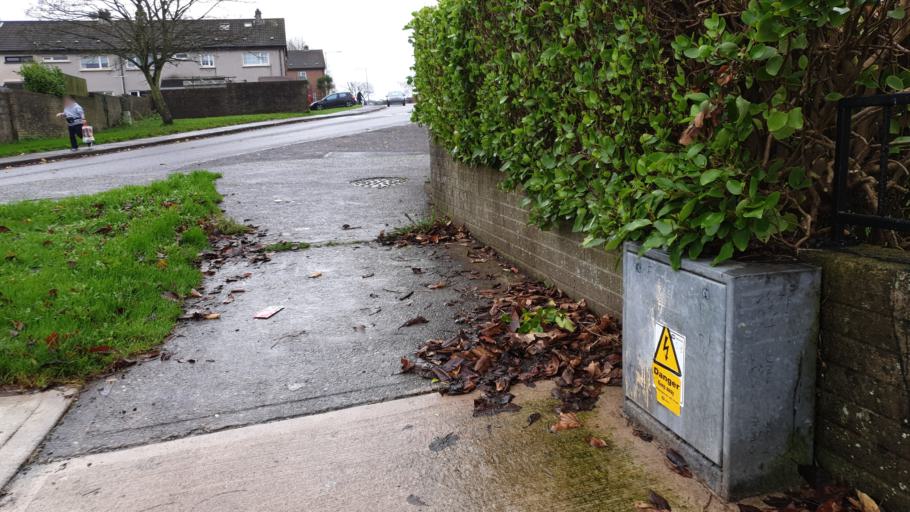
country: IE
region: Munster
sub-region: County Cork
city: Passage West
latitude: 51.8967
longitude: -8.4010
